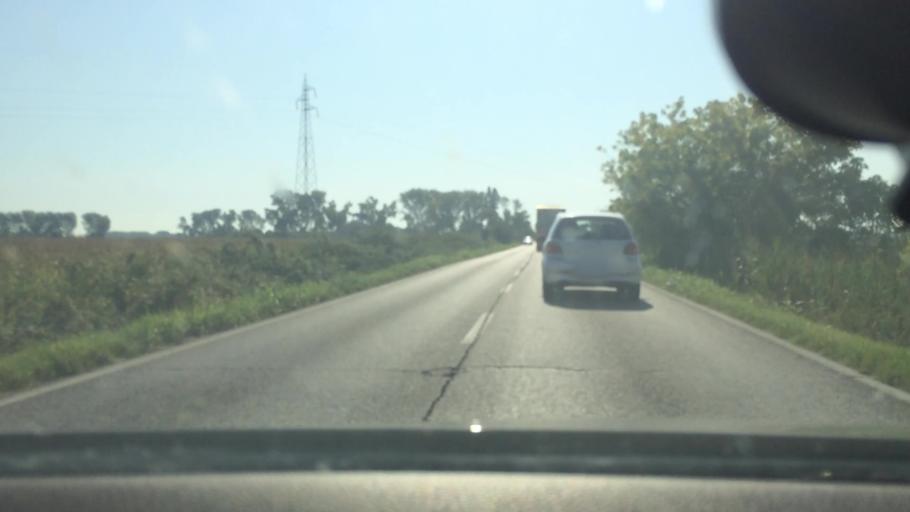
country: IT
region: Emilia-Romagna
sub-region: Provincia di Ferrara
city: Comacchio
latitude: 44.6912
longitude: 12.2001
